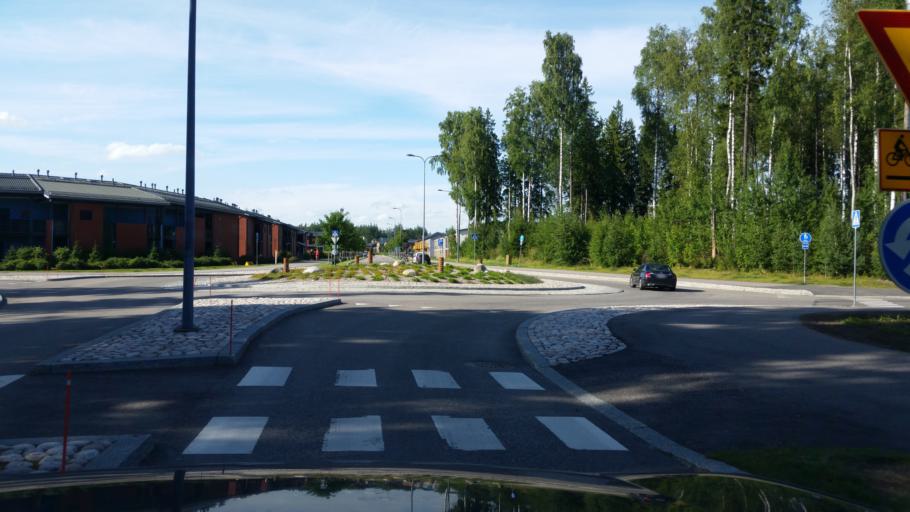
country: FI
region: Uusimaa
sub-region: Helsinki
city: Vantaa
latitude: 60.3334
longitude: 25.0275
